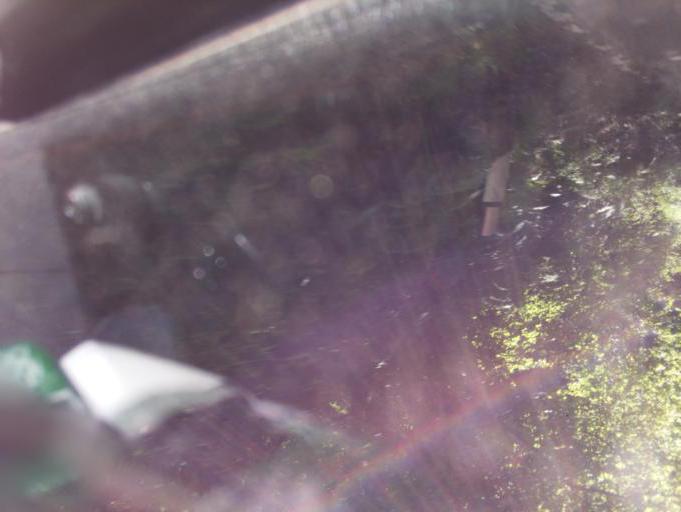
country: GB
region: England
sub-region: Gloucestershire
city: Cinderford
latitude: 51.7779
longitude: -2.5097
